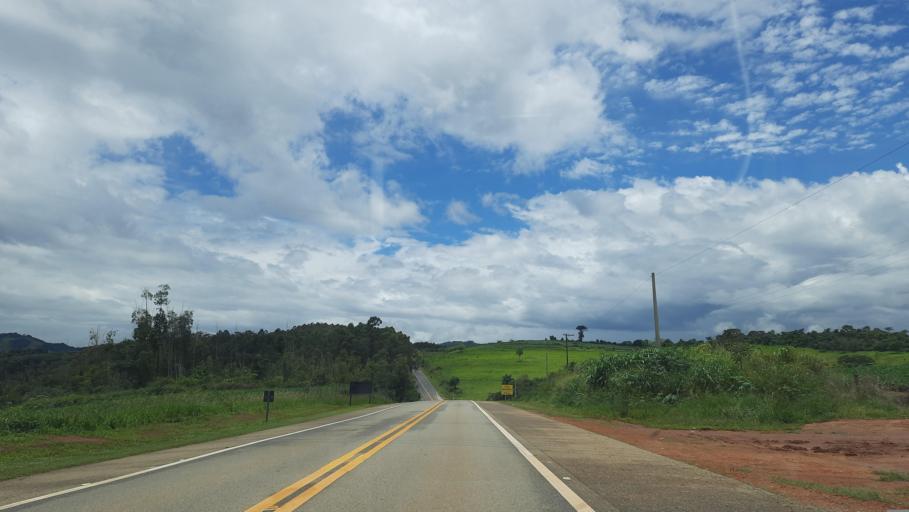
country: BR
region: Sao Paulo
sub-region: Vargem Grande Do Sul
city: Vargem Grande do Sul
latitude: -21.8006
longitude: -46.8061
